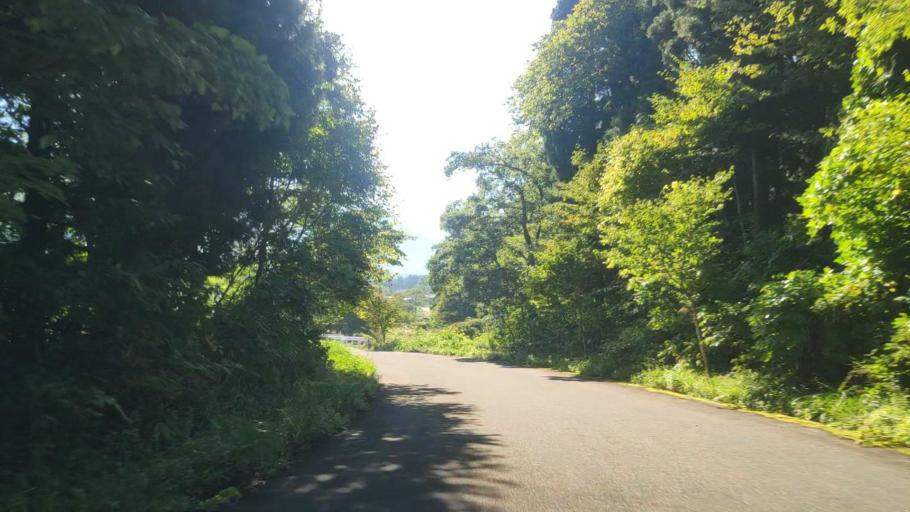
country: JP
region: Nagano
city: Iiyama
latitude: 36.8049
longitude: 138.4290
